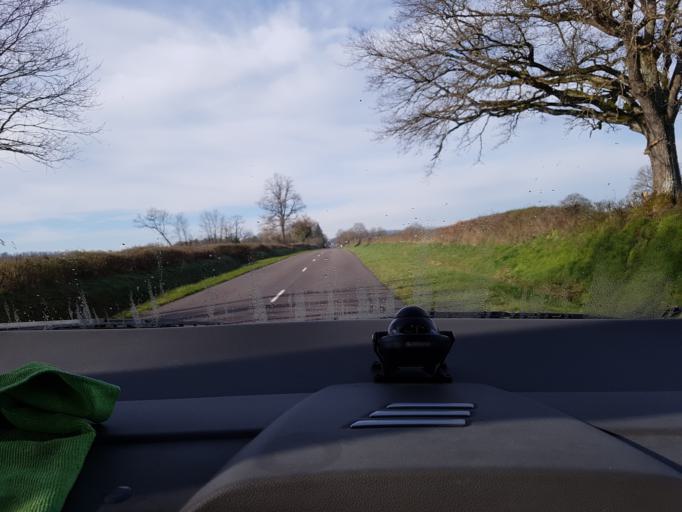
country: FR
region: Bourgogne
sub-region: Departement de Saone-et-Loire
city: Etang-sur-Arroux
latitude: 46.8313
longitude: 4.1824
